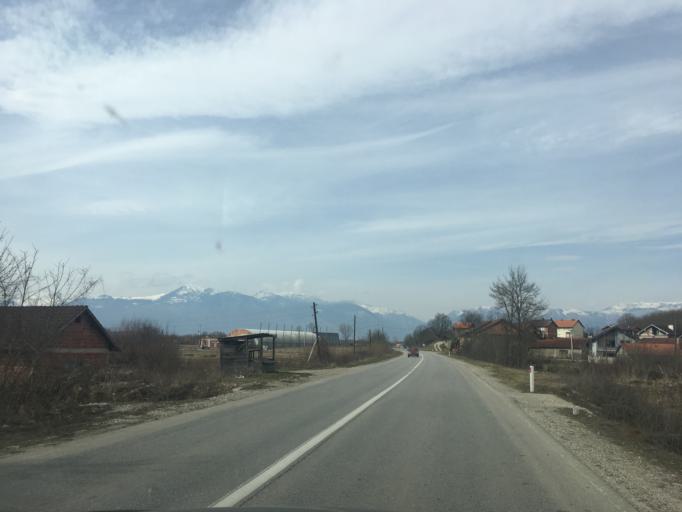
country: XK
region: Pec
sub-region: Komuna e Pejes
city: Kosuriq
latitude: 42.6228
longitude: 20.4718
